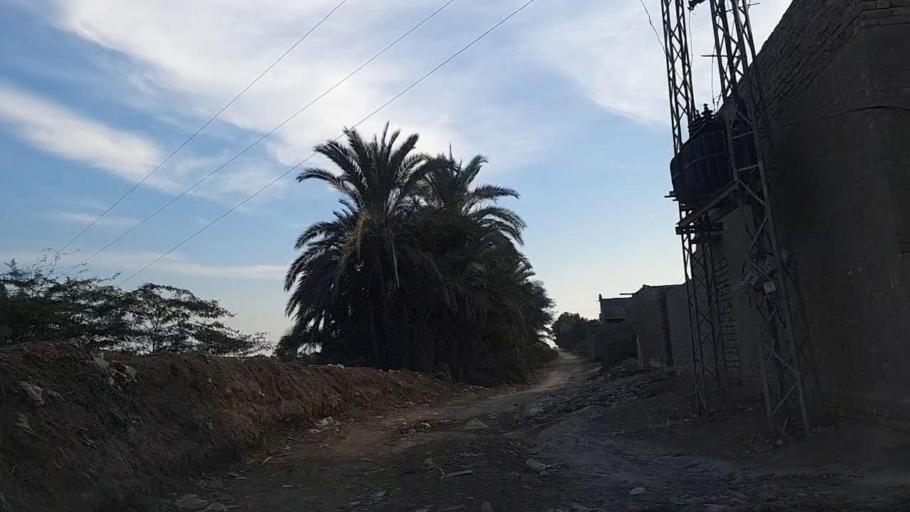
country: PK
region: Sindh
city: Bandhi
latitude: 26.5616
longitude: 68.2786
